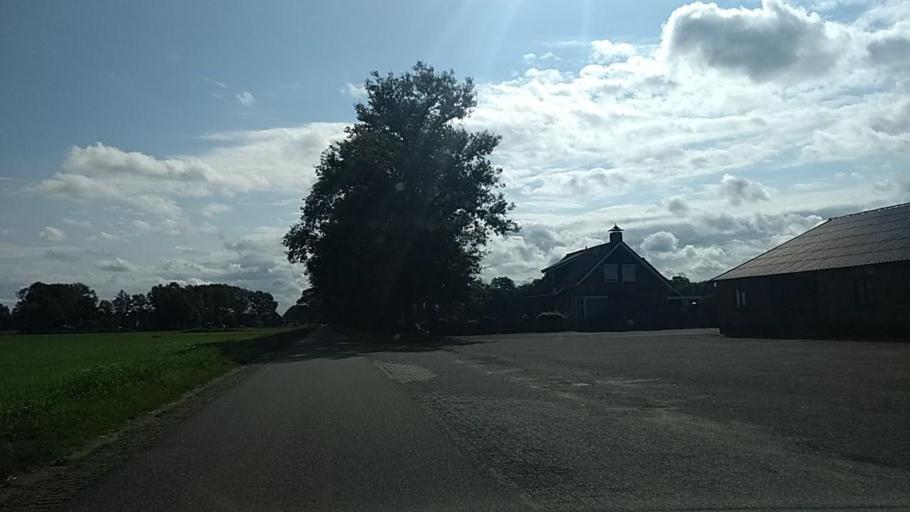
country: DE
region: Lower Saxony
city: Nordhorn
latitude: 52.3693
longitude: 7.0283
